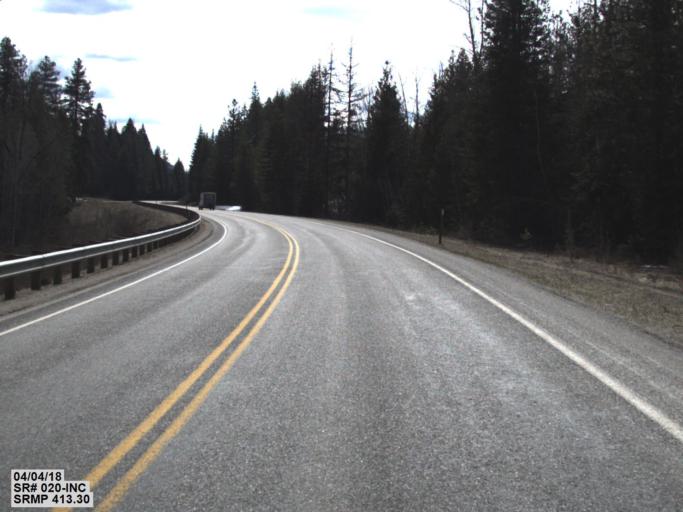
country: US
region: Washington
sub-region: Pend Oreille County
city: Newport
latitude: 48.4178
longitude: -117.3184
